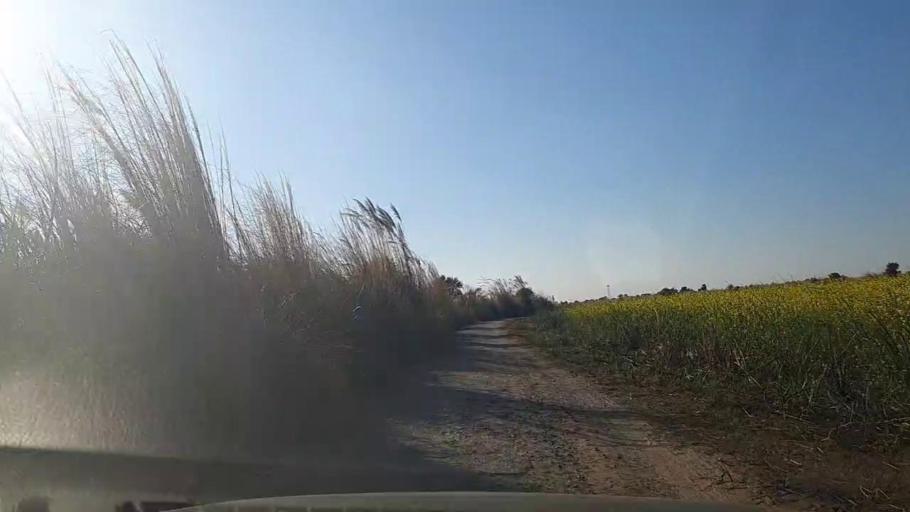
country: PK
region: Sindh
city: Khadro
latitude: 26.2413
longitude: 68.8664
